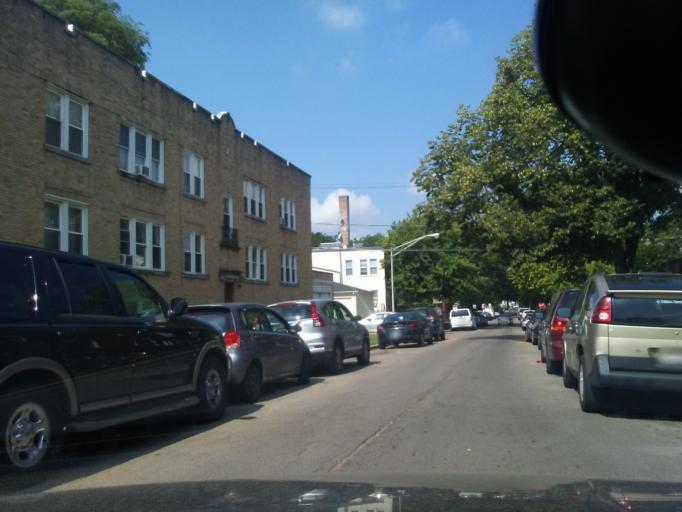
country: US
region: Illinois
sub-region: Cook County
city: Oak Park
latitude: 41.9187
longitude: -87.7524
